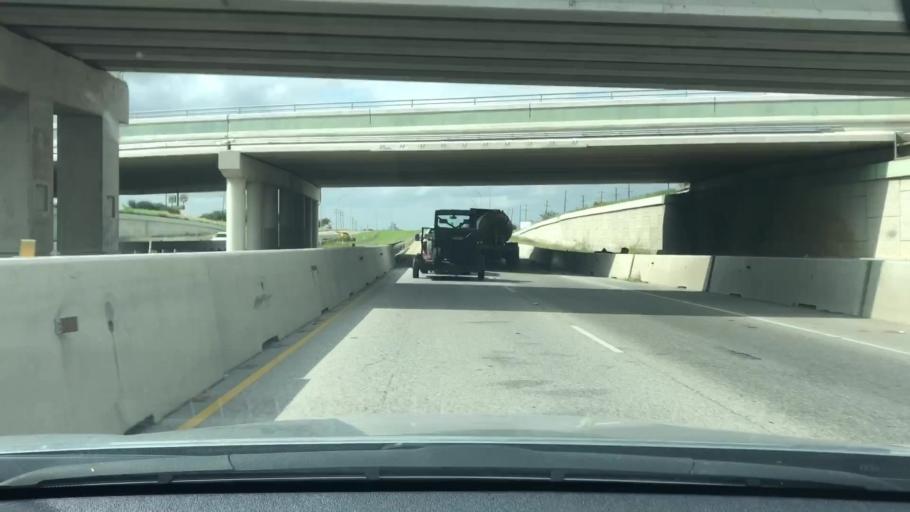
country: US
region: Texas
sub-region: Bexar County
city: Kirby
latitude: 29.4454
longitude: -98.3606
